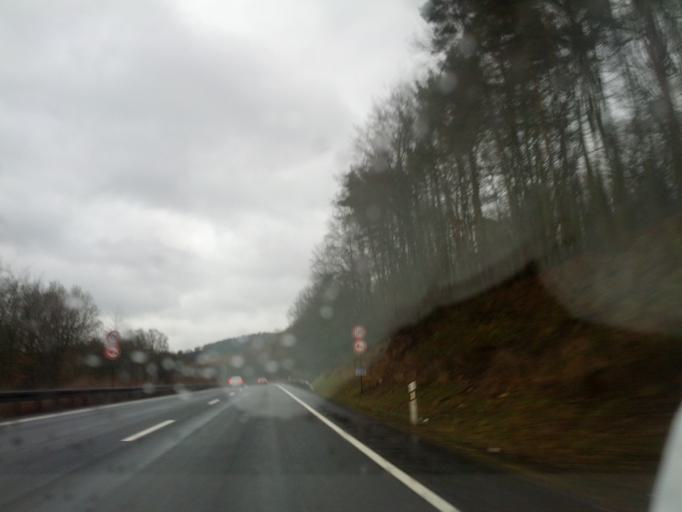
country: DE
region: Hesse
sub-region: Regierungsbezirk Kassel
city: Bad Hersfeld
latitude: 50.8573
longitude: 9.7600
